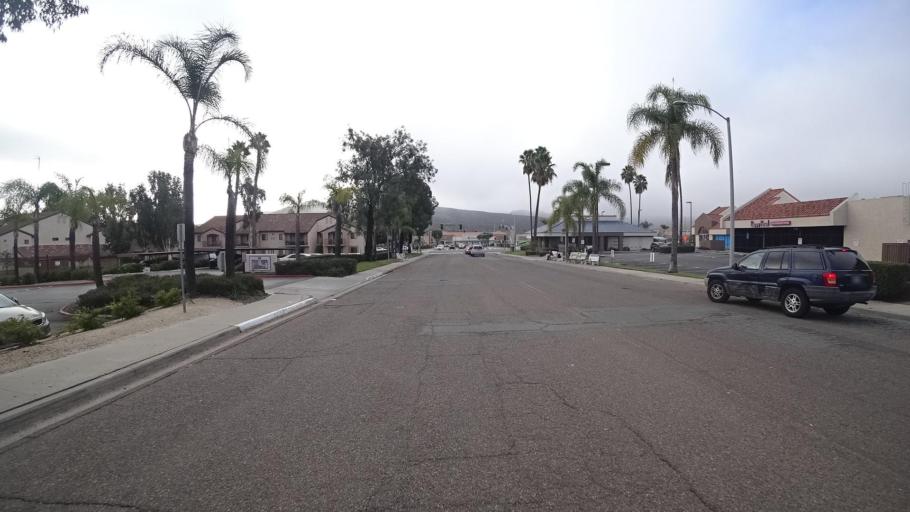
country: US
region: California
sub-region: San Diego County
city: Rancho San Diego
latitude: 32.7418
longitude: -116.9394
